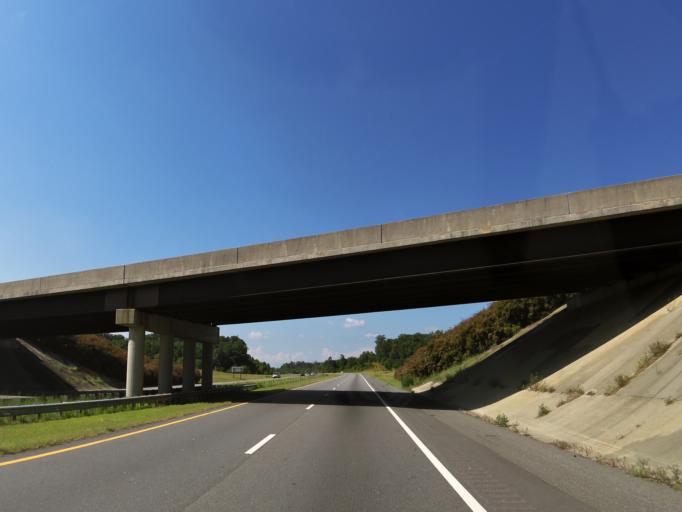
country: US
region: North Carolina
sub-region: Catawba County
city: Mountain View
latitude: 35.6793
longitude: -81.3399
